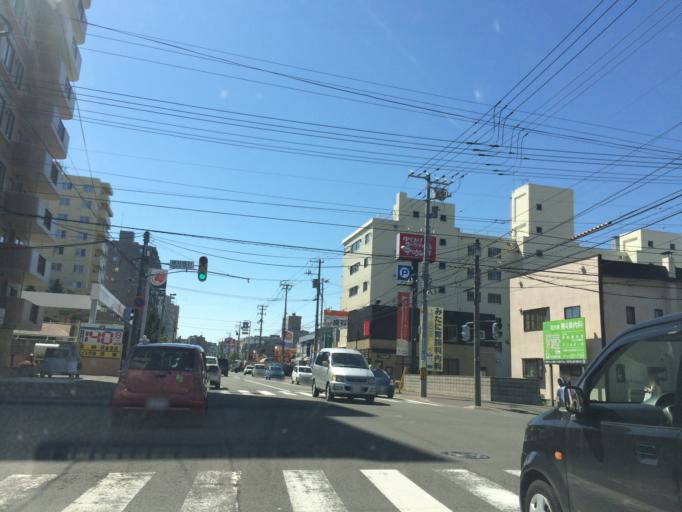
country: JP
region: Hokkaido
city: Sapporo
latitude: 43.0433
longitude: 141.3254
